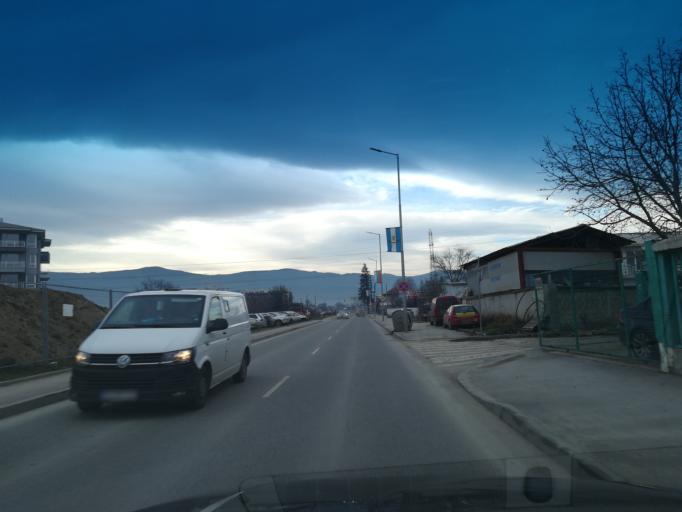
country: BG
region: Plovdiv
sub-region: Obshtina Plovdiv
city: Plovdiv
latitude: 42.1133
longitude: 24.7103
